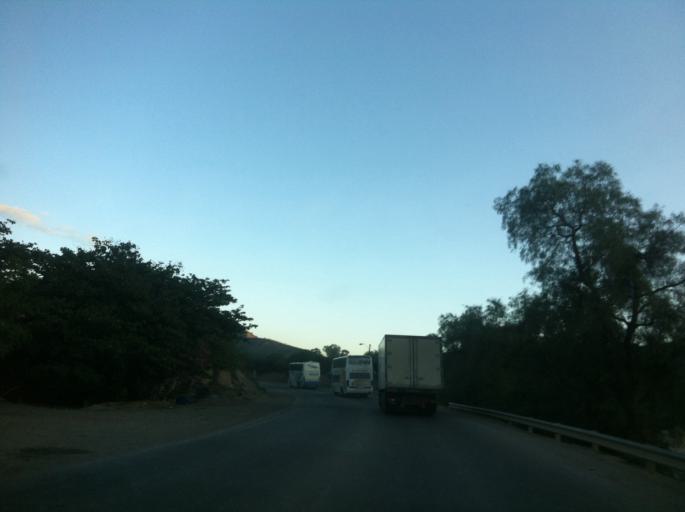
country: BO
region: Cochabamba
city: Sipe Sipe
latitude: -17.5586
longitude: -66.3419
